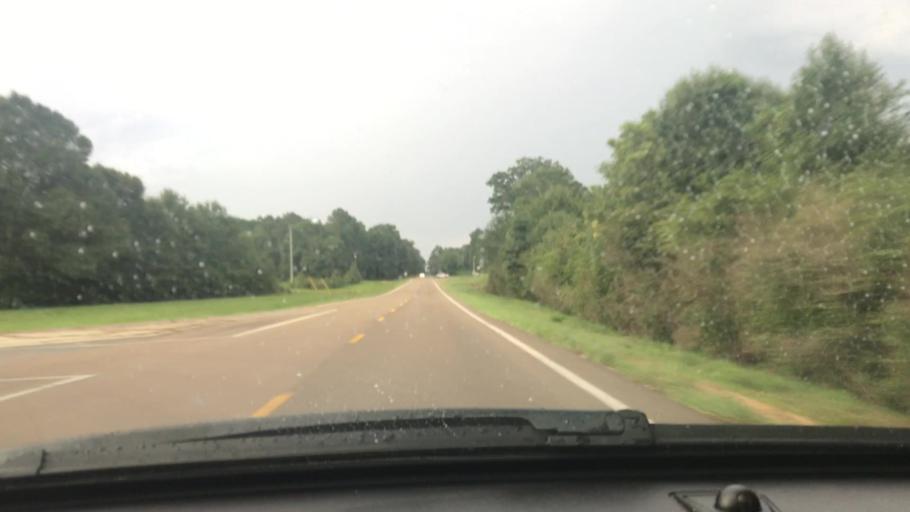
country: US
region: Mississippi
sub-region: Pike County
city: Summit
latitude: 31.3533
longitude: -90.6081
